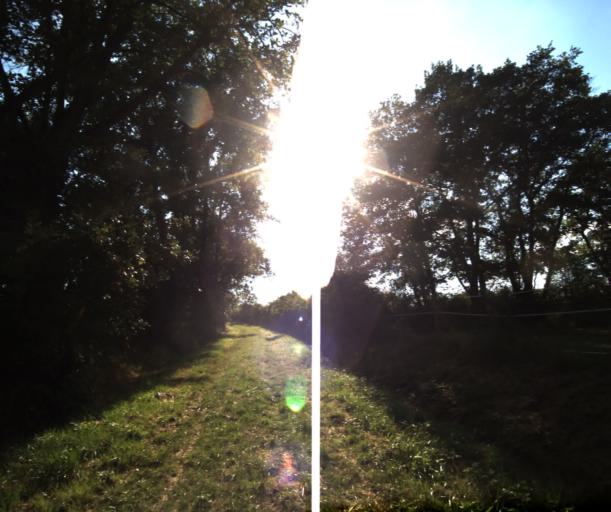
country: FR
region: Midi-Pyrenees
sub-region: Departement de la Haute-Garonne
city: Lherm
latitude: 43.4691
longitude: 1.2041
